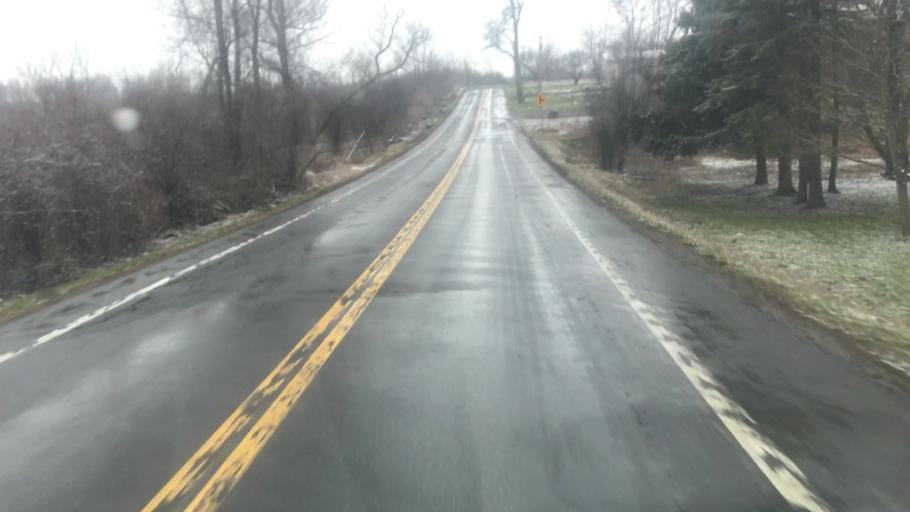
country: US
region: New York
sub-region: Onondaga County
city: Skaneateles
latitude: 42.9943
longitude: -76.4013
